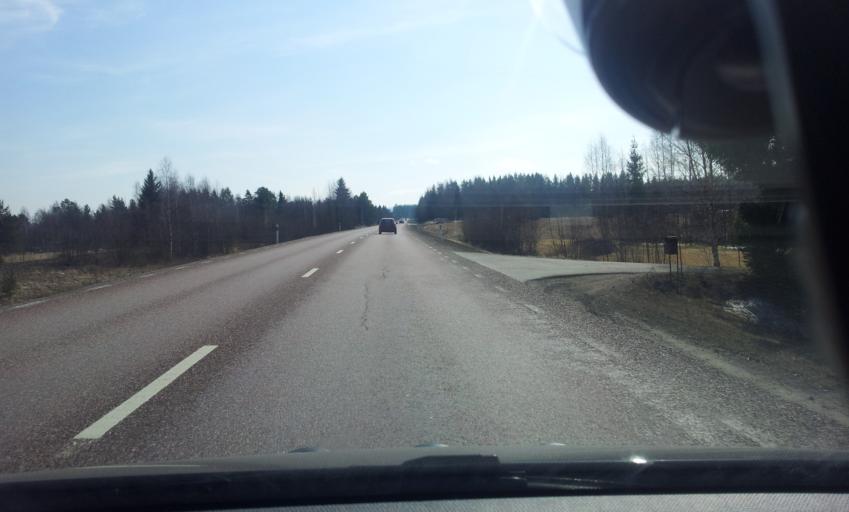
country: SE
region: Gaevleborg
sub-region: Ljusdals Kommun
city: Jaervsoe
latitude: 61.7806
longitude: 16.1414
